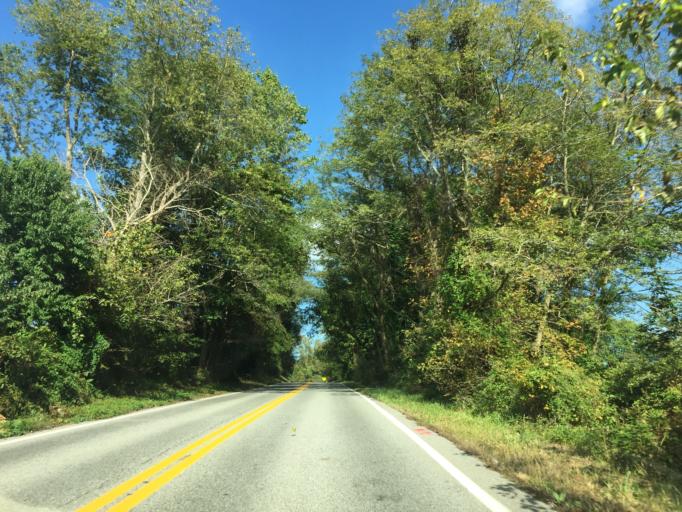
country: US
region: Maryland
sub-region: Harford County
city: Fallston
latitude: 39.4997
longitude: -76.4660
